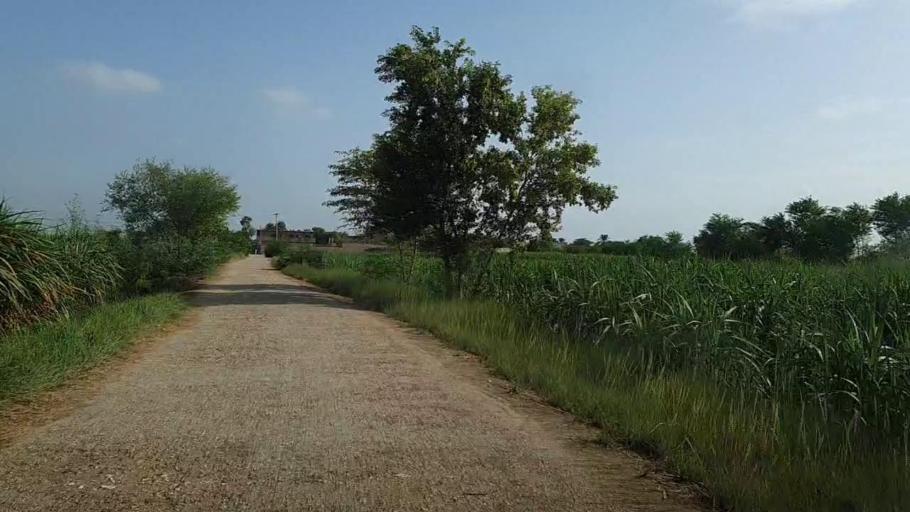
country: PK
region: Sindh
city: Bhiria
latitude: 26.8432
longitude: 68.2396
